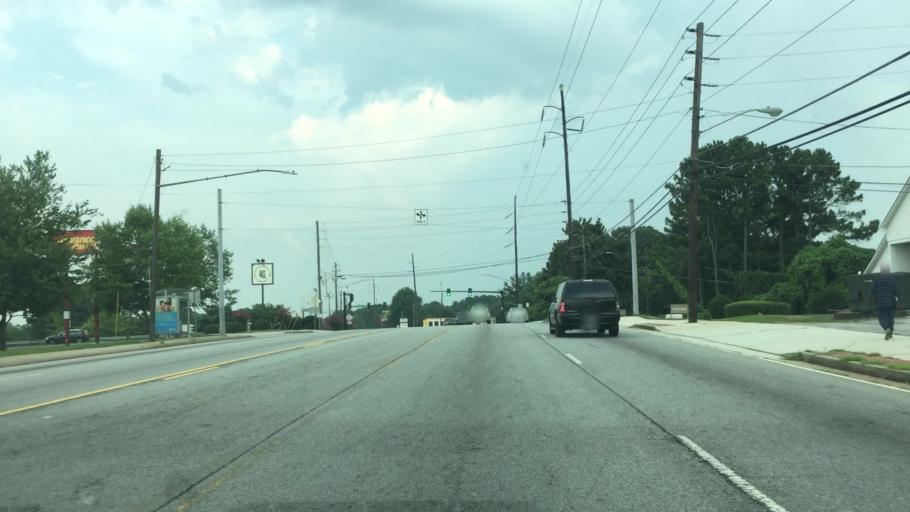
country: US
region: Georgia
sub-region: DeKalb County
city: Belvedere Park
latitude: 33.7568
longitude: -84.2385
